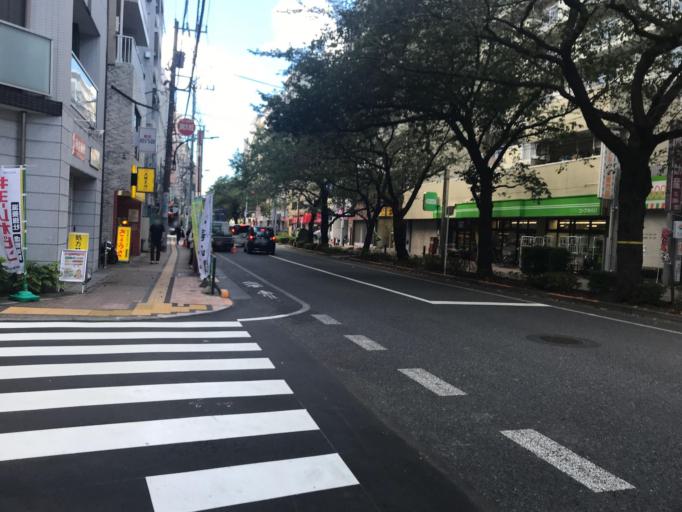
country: JP
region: Tokyo
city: Tokyo
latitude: 35.7381
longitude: 139.6622
